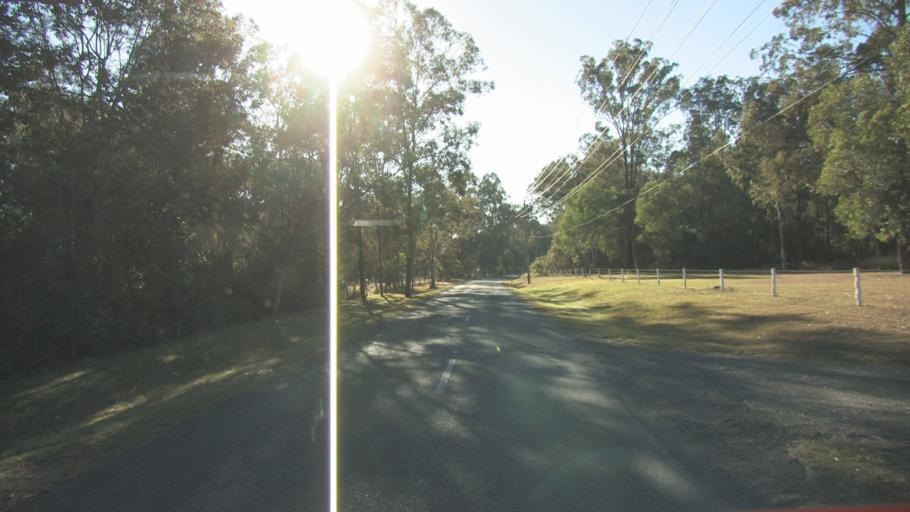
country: AU
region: Queensland
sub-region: Logan
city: North Maclean
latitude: -27.7841
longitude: 152.9721
